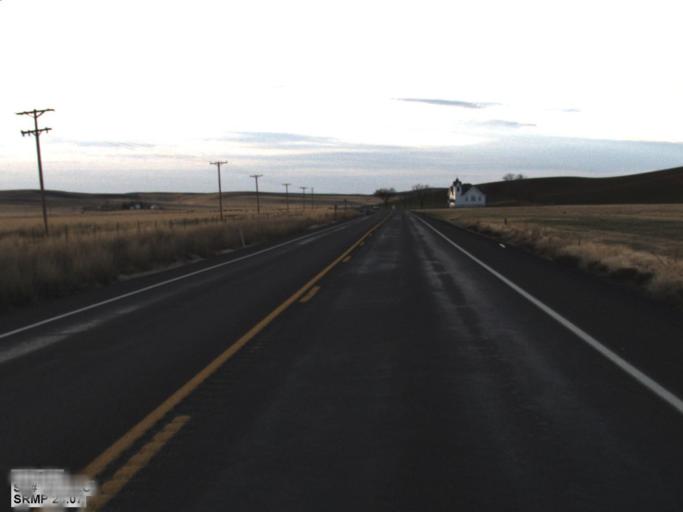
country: US
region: Washington
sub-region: Garfield County
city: Pomeroy
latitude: 46.7816
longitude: -117.7008
